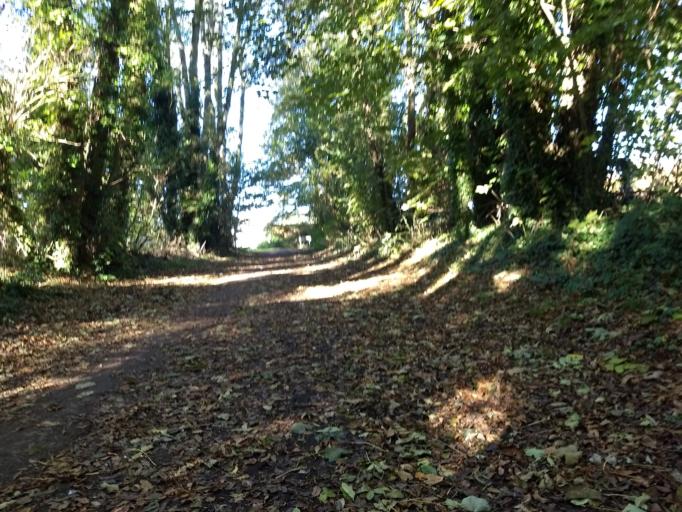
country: GB
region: England
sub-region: Isle of Wight
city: Newport
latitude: 50.6732
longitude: -1.2837
